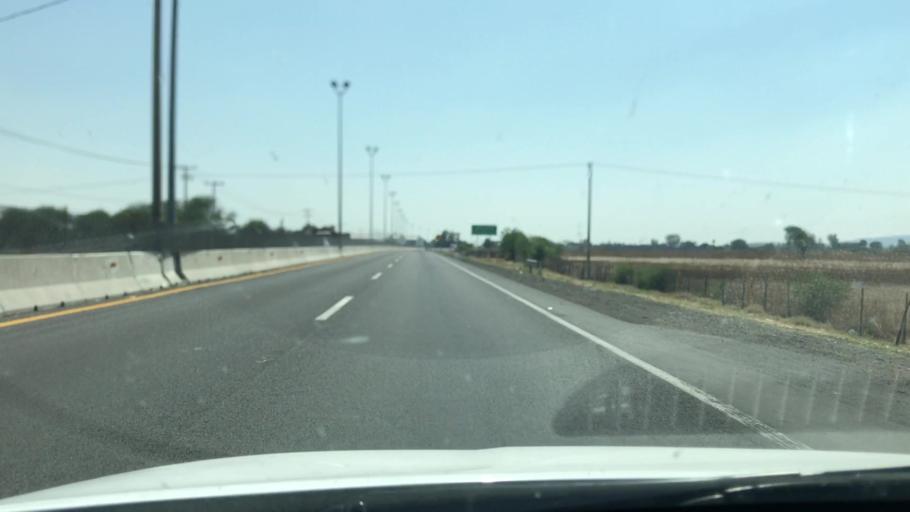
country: MX
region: Guanajuato
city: Abasolo
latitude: 20.4625
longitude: -101.5227
